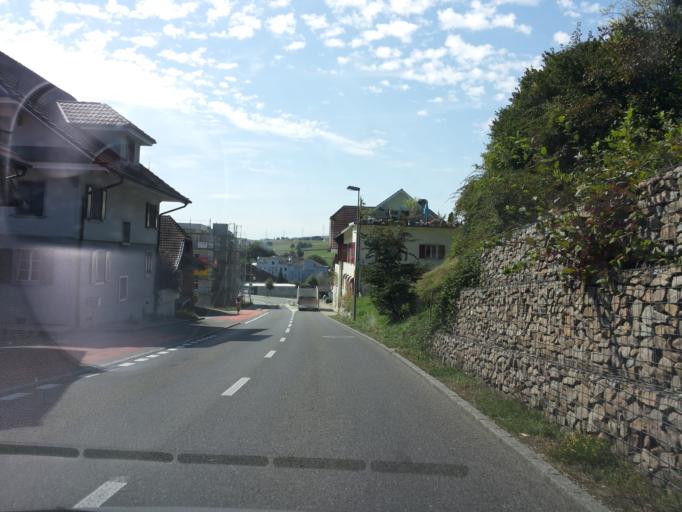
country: CH
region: Lucerne
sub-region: Willisau District
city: Pfaffnau
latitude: 47.2312
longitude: 7.9029
